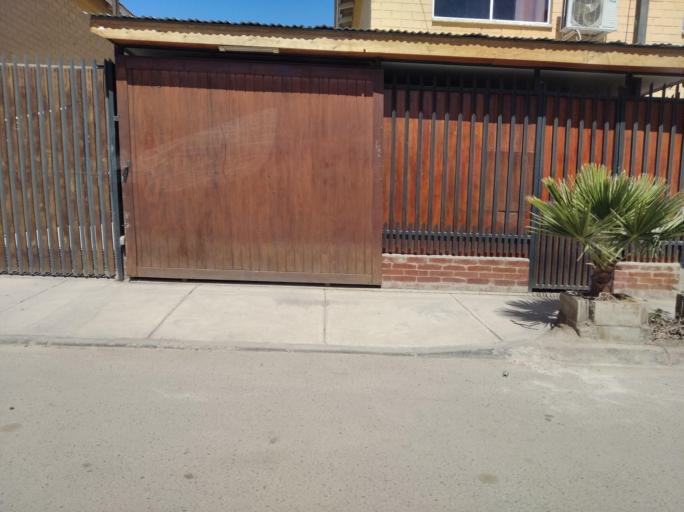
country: CL
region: Atacama
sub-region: Provincia de Copiapo
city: Copiapo
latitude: -27.4097
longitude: -70.2831
